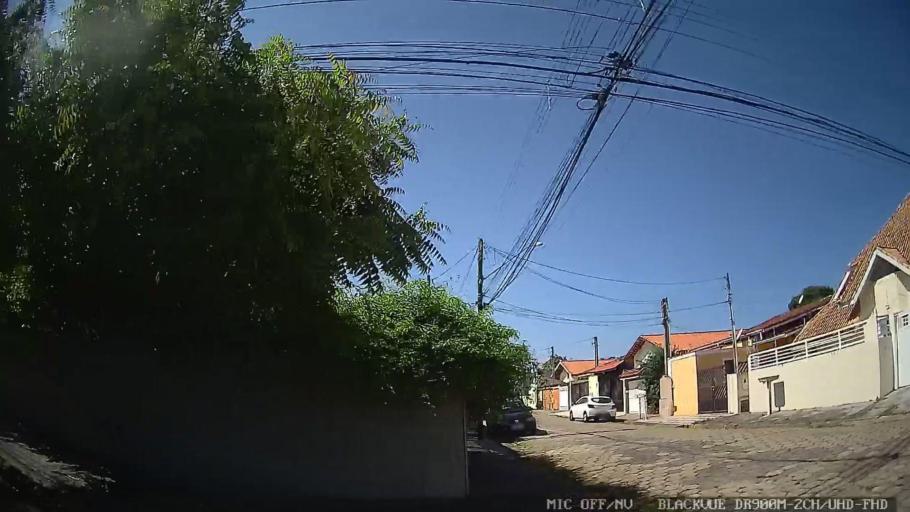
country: BR
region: Sao Paulo
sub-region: Peruibe
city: Peruibe
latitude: -24.3106
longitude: -46.9954
